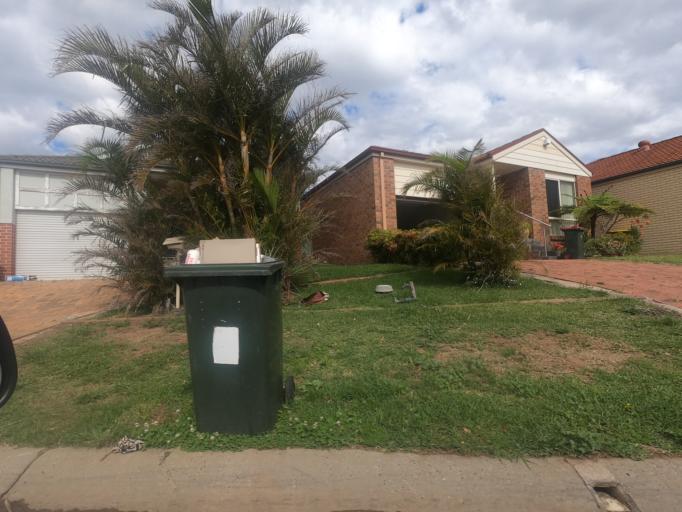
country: AU
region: New South Wales
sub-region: Wollongong
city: Dapto
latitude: -34.4861
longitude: 150.7767
